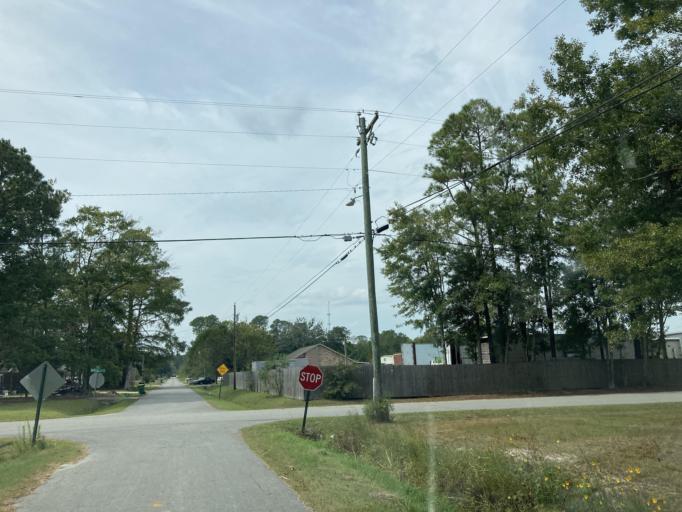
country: US
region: Mississippi
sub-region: Jackson County
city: Gulf Hills
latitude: 30.4516
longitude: -88.8495
